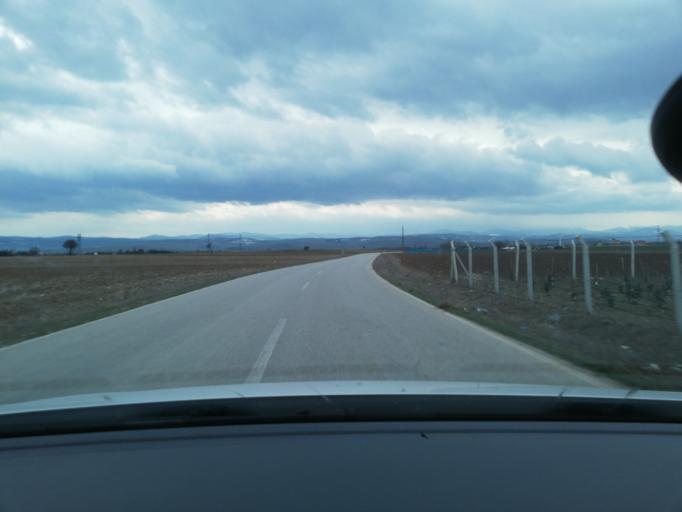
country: TR
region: Bolu
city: Gerede
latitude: 40.7678
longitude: 32.2016
